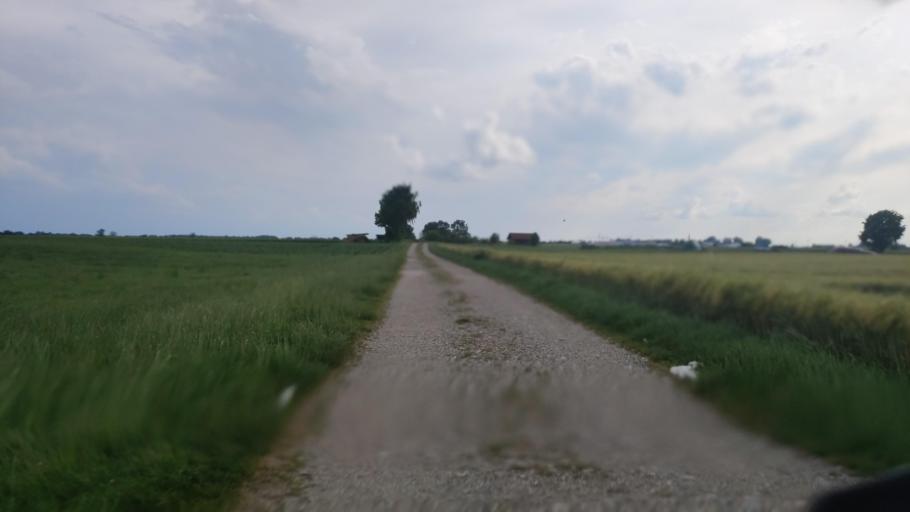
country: DE
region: Bavaria
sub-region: Swabia
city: Oberottmarshausen
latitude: 48.2312
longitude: 10.8616
